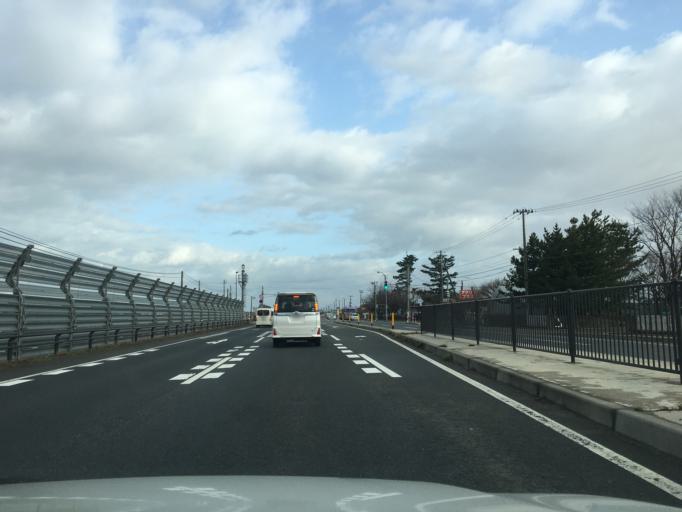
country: JP
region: Yamagata
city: Sakata
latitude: 38.8576
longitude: 139.8457
